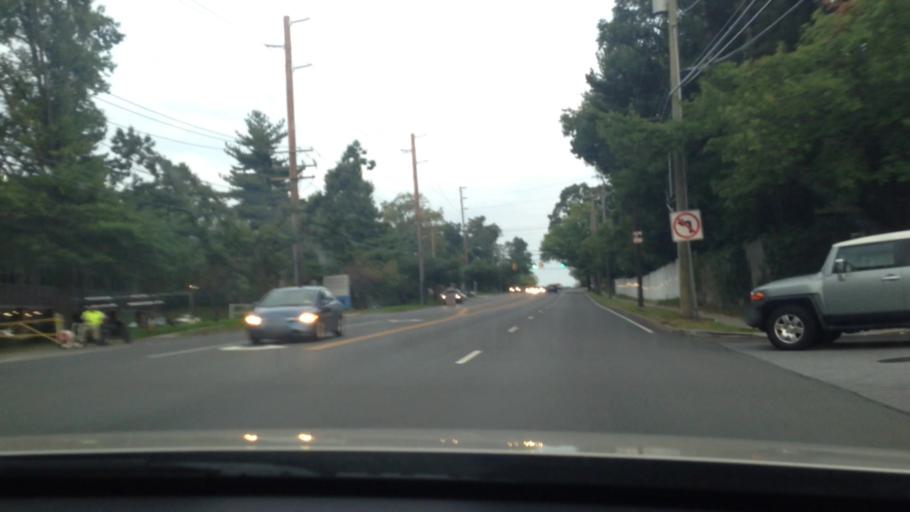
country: US
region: New York
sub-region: Nassau County
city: Manhasset Hills
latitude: 40.7624
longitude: -73.6894
